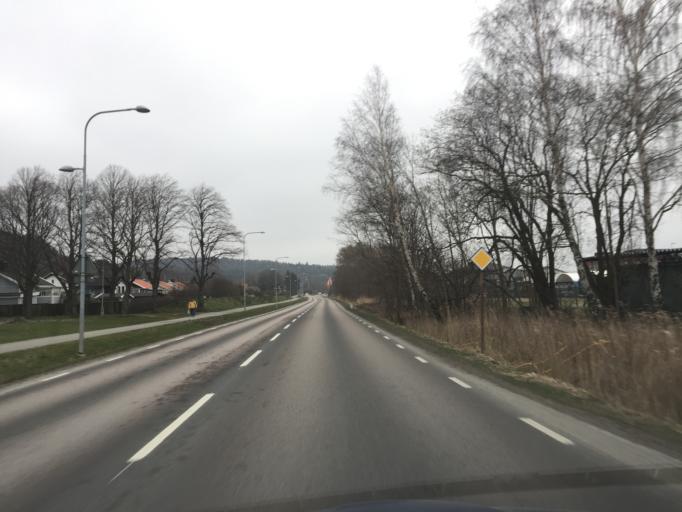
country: SE
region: Vaestra Goetaland
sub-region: Partille Kommun
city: Partille
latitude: 57.7396
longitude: 12.0712
